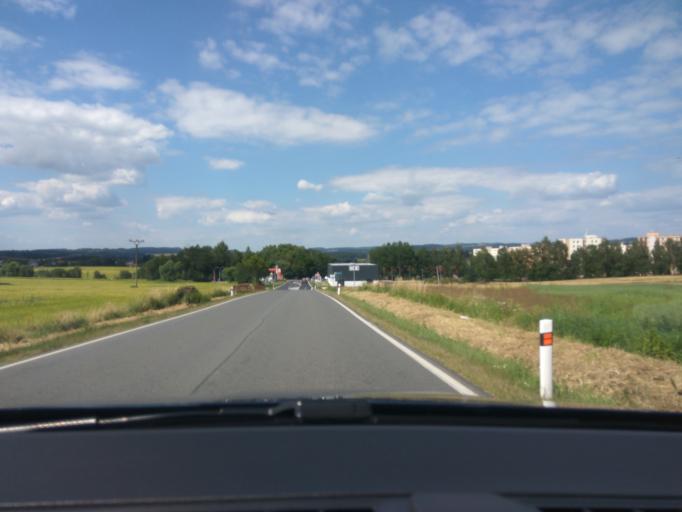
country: CZ
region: Jihocesky
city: Milevsko
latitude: 49.4389
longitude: 14.3586
